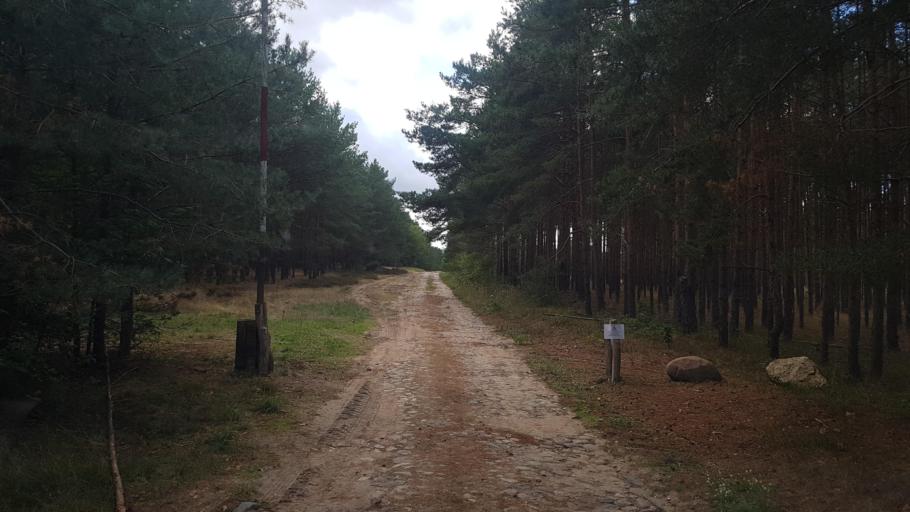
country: DE
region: Brandenburg
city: Treuenbrietzen
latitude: 52.0709
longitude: 12.8017
